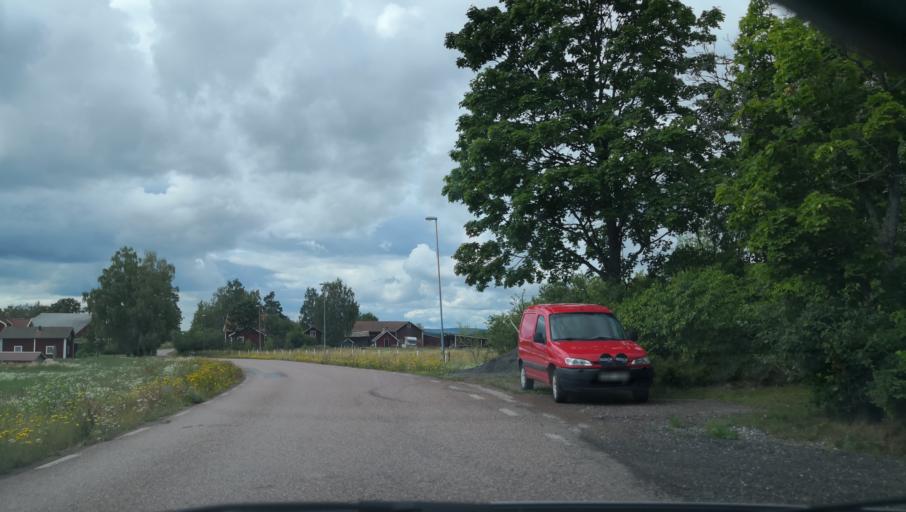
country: SE
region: Dalarna
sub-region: Borlange Kommun
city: Ornas
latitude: 60.4433
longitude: 15.5891
